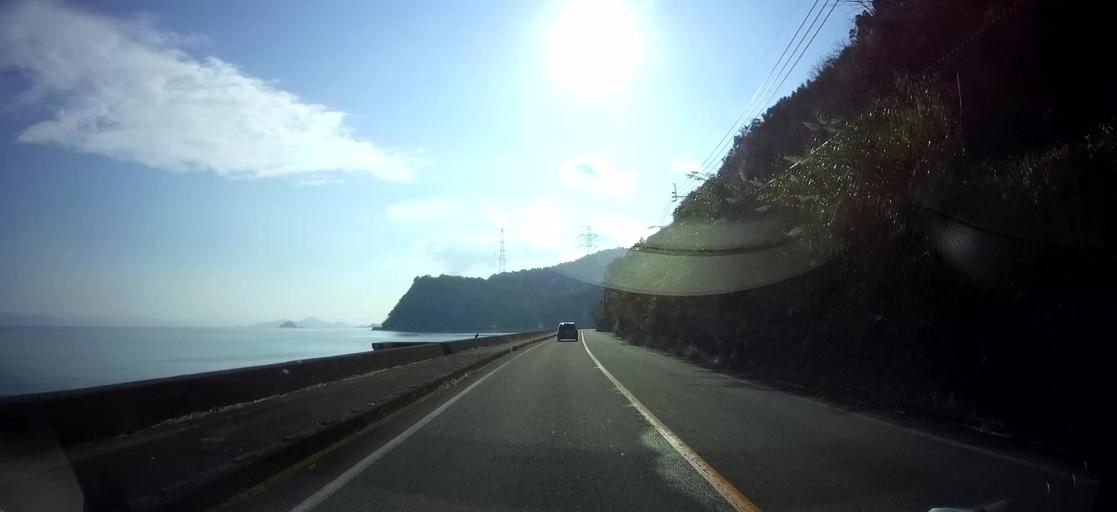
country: JP
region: Kumamoto
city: Yatsushiro
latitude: 32.5138
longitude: 130.4550
